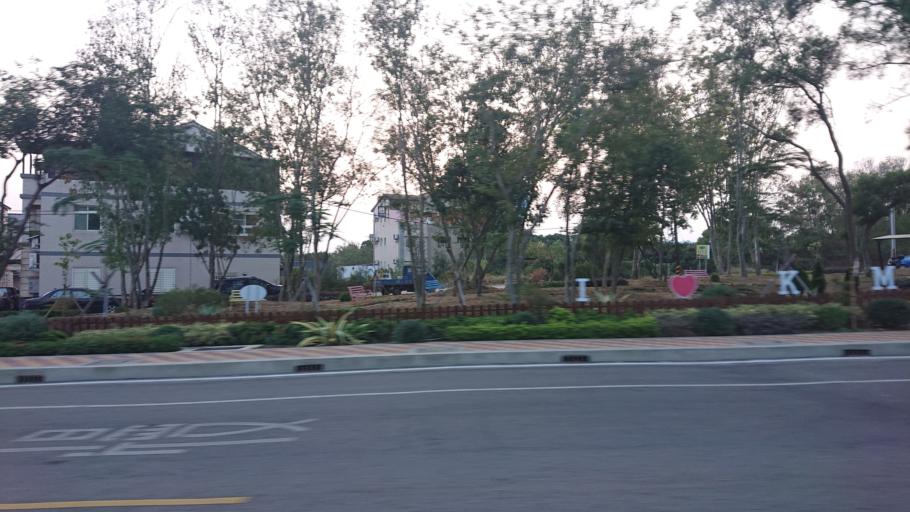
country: TW
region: Fukien
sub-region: Kinmen
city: Jincheng
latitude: 24.4436
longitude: 118.3199
